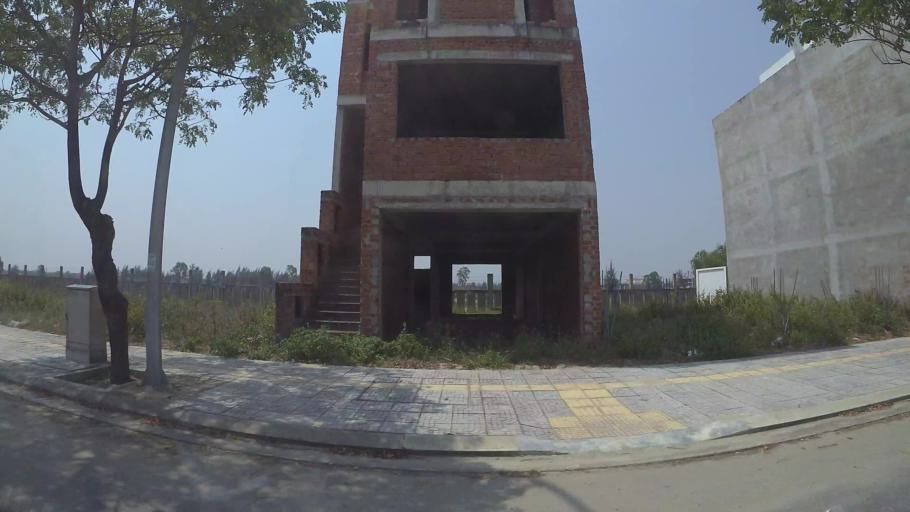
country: VN
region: Da Nang
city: Ngu Hanh Son
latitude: 15.9732
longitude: 108.2609
